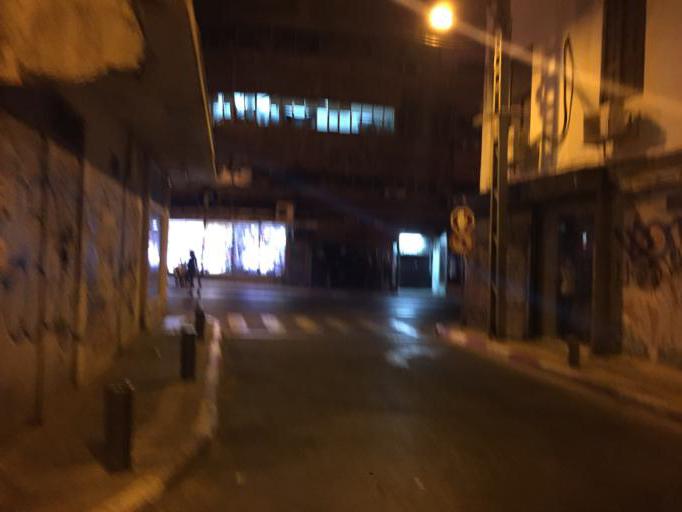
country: IL
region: Tel Aviv
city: Yafo
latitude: 32.0608
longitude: 34.7708
